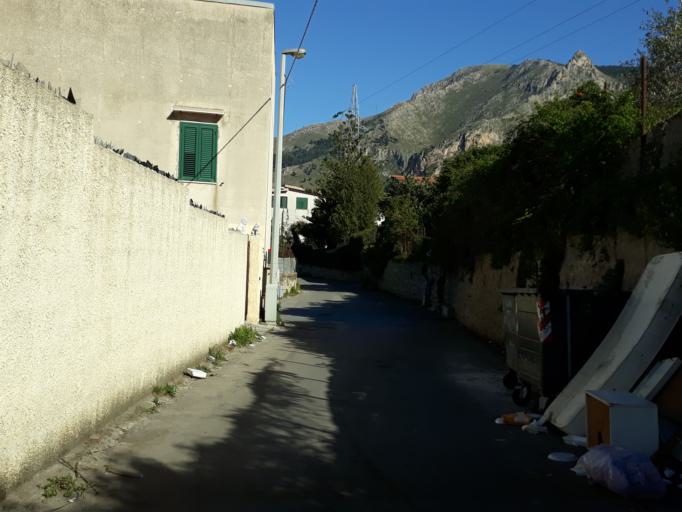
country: IT
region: Sicily
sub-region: Palermo
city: Villa Ciambra
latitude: 38.0749
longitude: 13.3552
